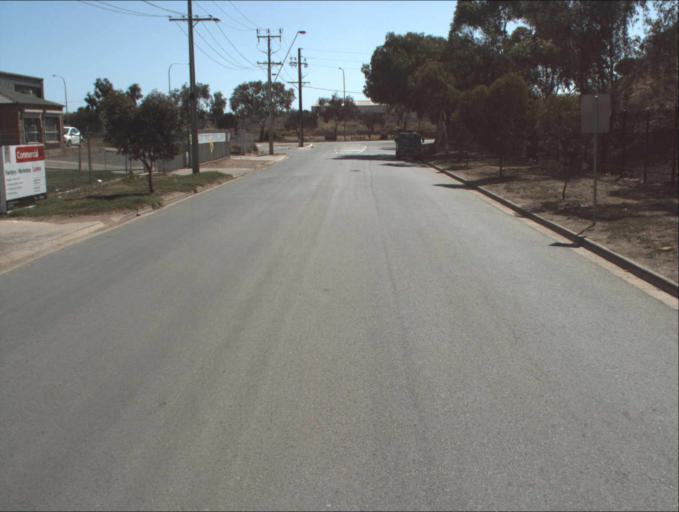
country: AU
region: South Australia
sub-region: Port Adelaide Enfield
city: Alberton
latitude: -34.8367
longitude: 138.5472
